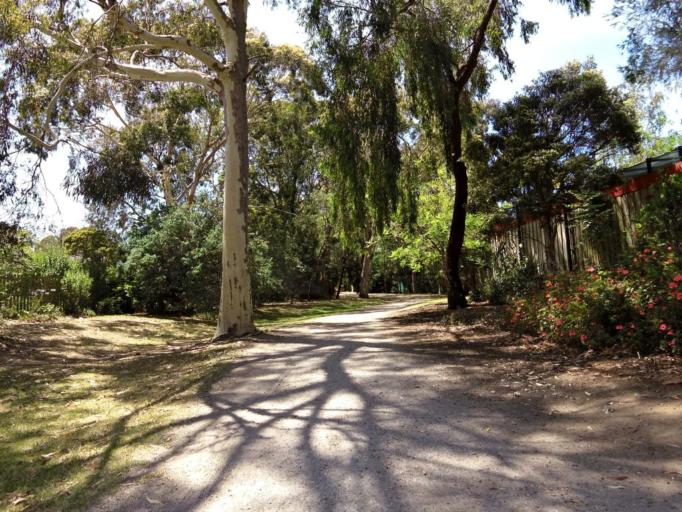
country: AU
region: Victoria
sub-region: Stonnington
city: Glen Iris
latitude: -37.8531
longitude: 145.0645
